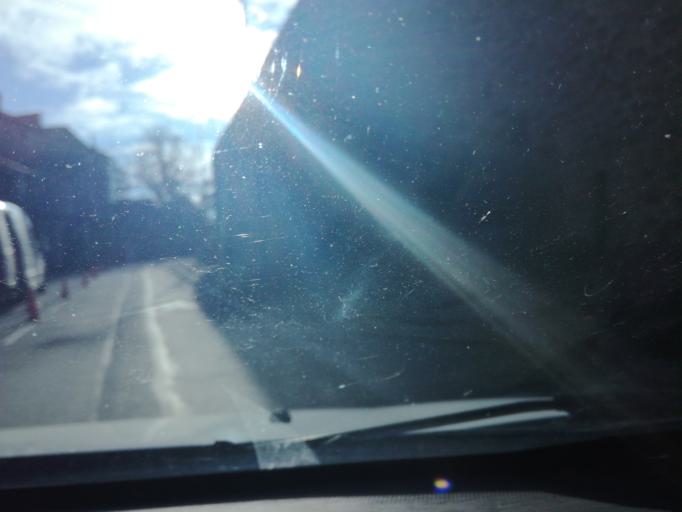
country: FR
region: Brittany
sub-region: Departement des Cotes-d'Armor
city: Dinan
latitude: 48.4523
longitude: -2.0391
